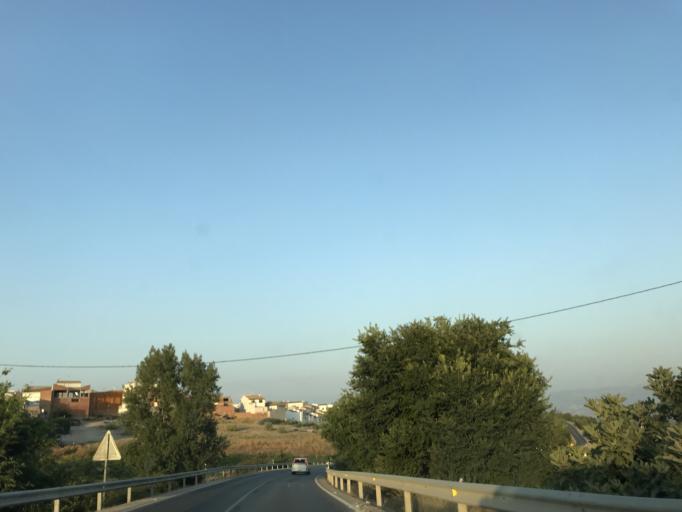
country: ES
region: Andalusia
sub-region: Provincia de Jaen
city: Torreperogil
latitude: 38.0313
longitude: -3.2958
